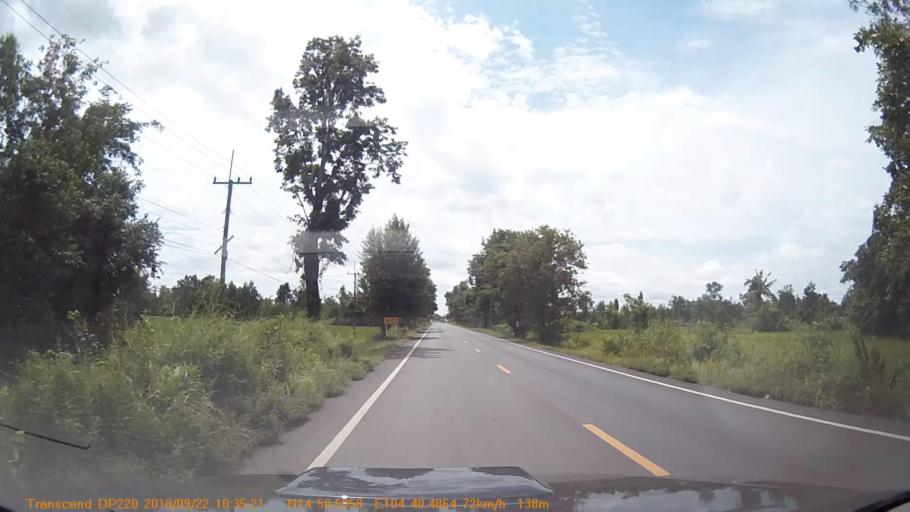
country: TH
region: Sisaket
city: Benchalak
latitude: 14.8434
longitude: 104.6747
